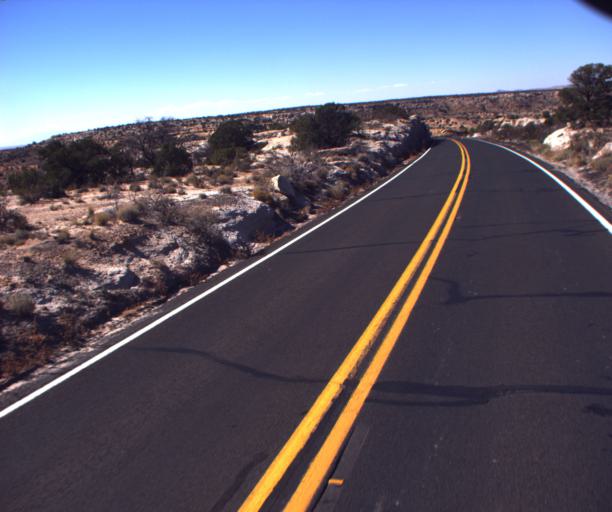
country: US
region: Arizona
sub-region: Navajo County
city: First Mesa
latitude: 35.8510
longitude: -110.5395
